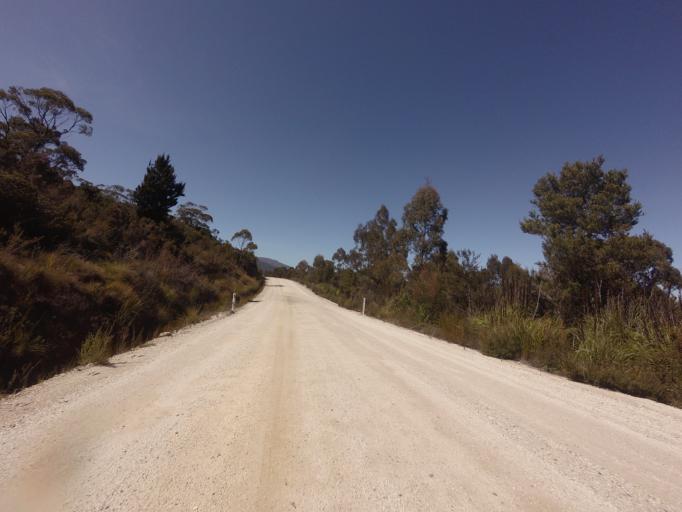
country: AU
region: Tasmania
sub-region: Huon Valley
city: Geeveston
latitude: -42.9427
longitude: 146.3485
